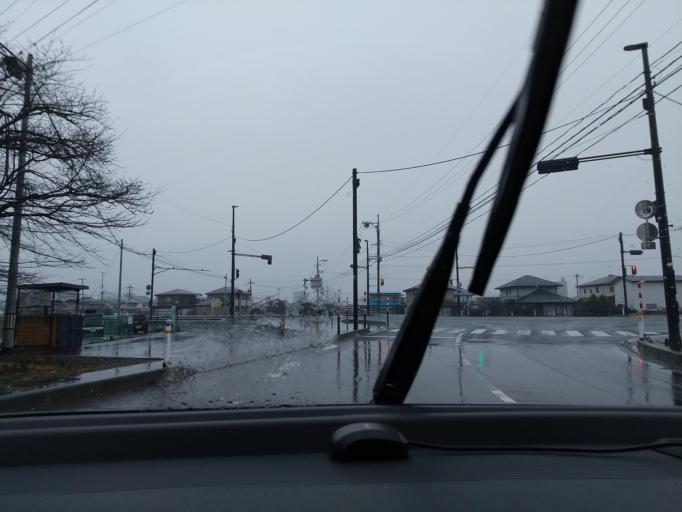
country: JP
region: Iwate
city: Morioka-shi
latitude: 39.6836
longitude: 141.1165
